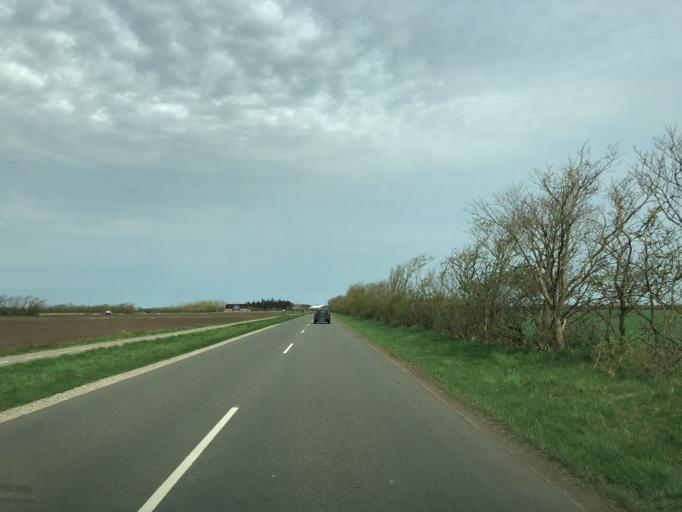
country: DK
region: Central Jutland
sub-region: Ringkobing-Skjern Kommune
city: Skjern
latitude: 55.9343
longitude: 8.4537
